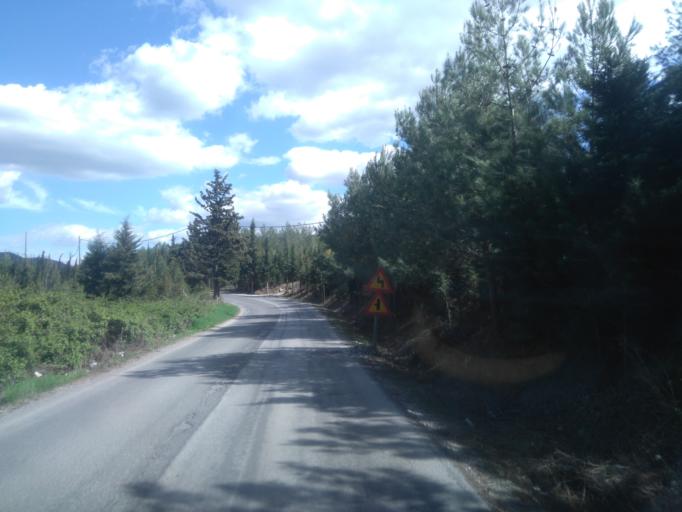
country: GR
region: Central Macedonia
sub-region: Nomos Thessalonikis
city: Pefka
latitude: 40.6428
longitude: 23.0014
